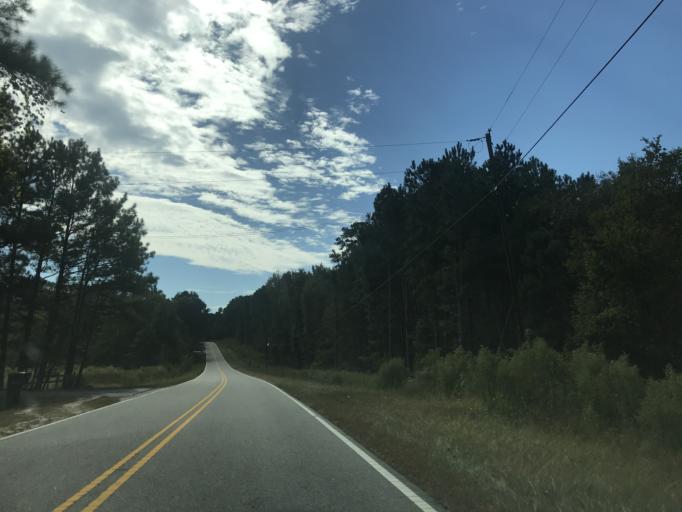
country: US
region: North Carolina
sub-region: Wake County
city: Rolesville
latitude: 35.8771
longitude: -78.4759
